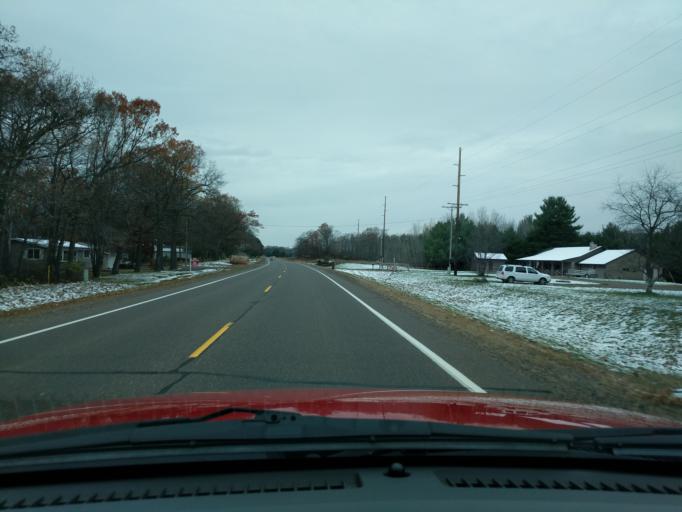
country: US
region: Wisconsin
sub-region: Burnett County
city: Siren
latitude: 45.8200
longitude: -92.2442
